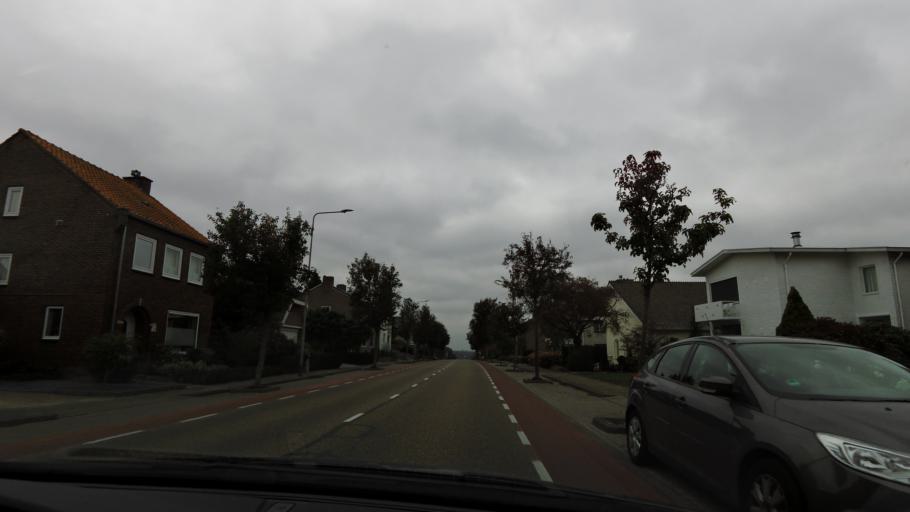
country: NL
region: Limburg
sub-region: Gemeente Schinnen
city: Puth
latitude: 50.9596
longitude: 5.8641
